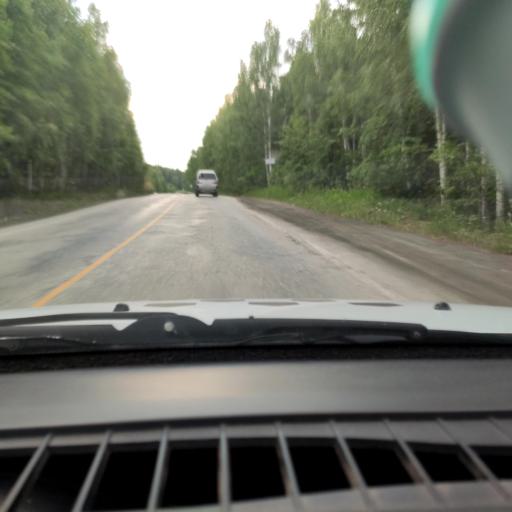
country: RU
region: Chelyabinsk
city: Karabash
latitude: 55.5234
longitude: 60.3351
